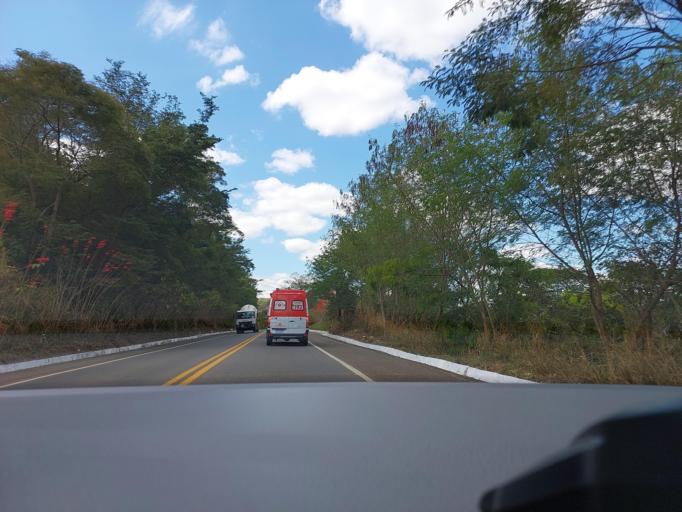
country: BR
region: Minas Gerais
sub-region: Muriae
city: Muriae
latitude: -21.1370
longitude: -42.3023
